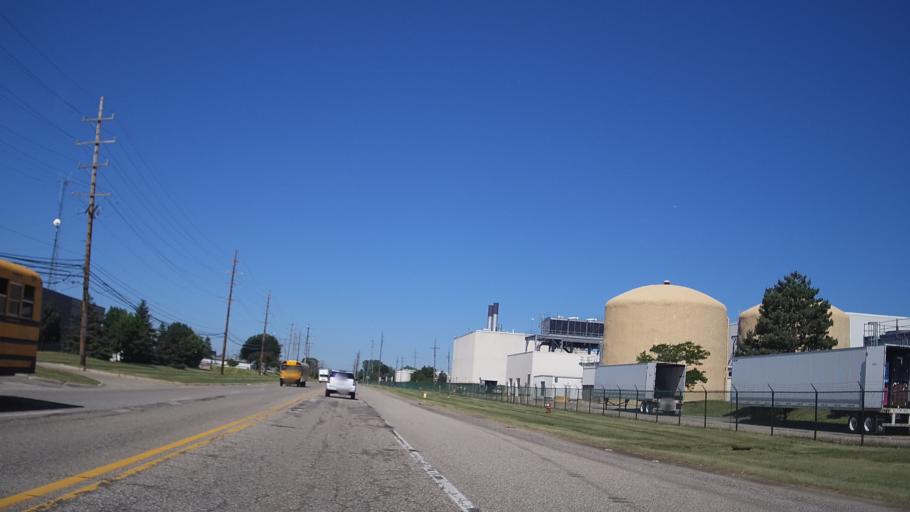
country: US
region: Michigan
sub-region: Macomb County
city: Sterling Heights
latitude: 42.5950
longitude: -83.0334
